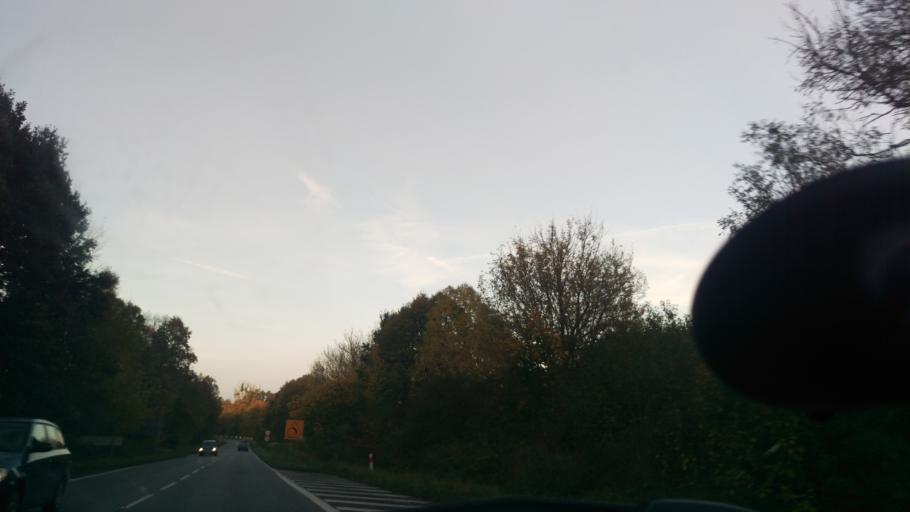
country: PL
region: West Pomeranian Voivodeship
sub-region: Powiat gryfinski
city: Stare Czarnowo
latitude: 53.2991
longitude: 14.7913
